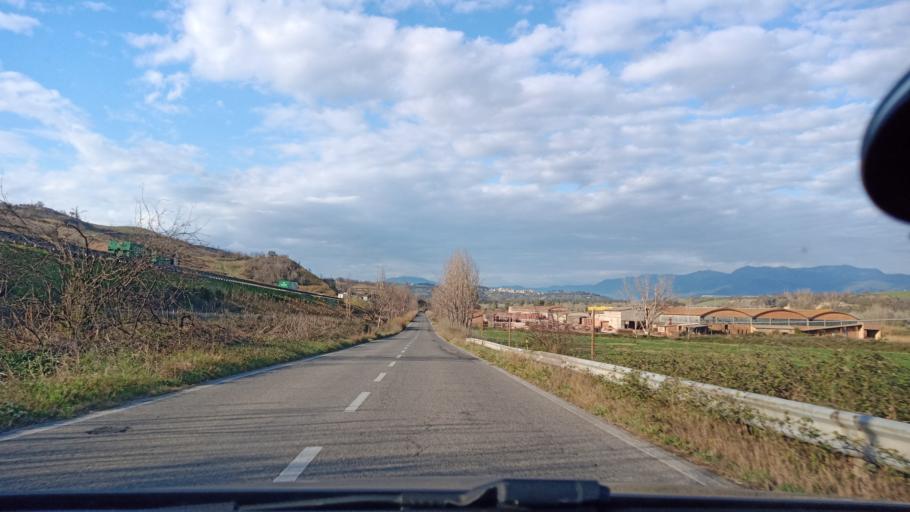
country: IT
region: Latium
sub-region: Citta metropolitana di Roma Capitale
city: Civitella San Paolo
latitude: 42.1893
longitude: 12.6038
